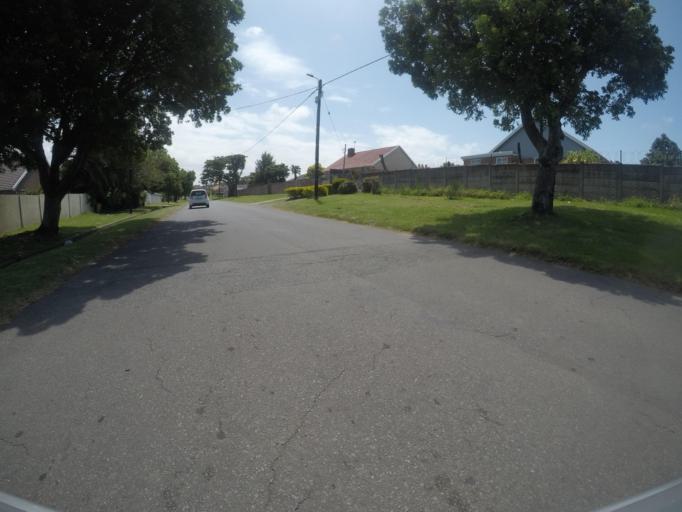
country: ZA
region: Eastern Cape
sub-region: Buffalo City Metropolitan Municipality
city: East London
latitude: -32.9724
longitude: 27.8711
